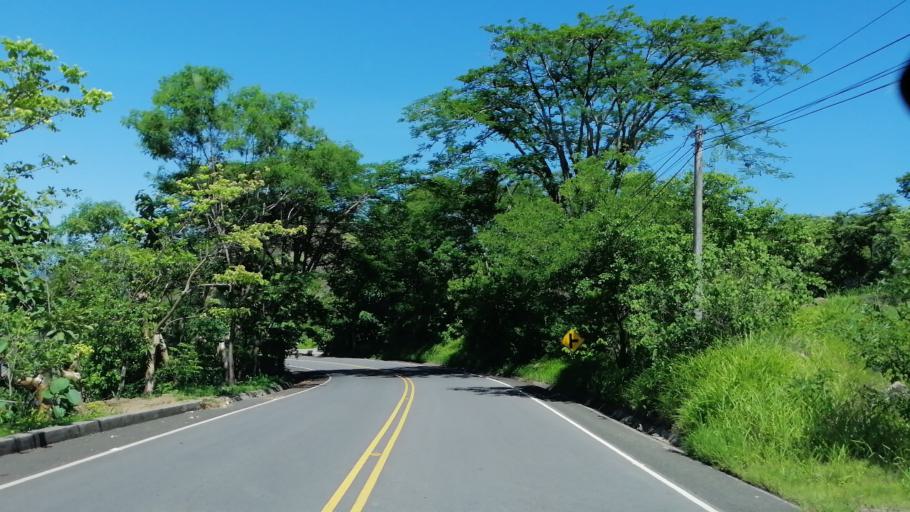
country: SV
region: Morazan
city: Cacaopera
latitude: 13.8119
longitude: -88.1697
